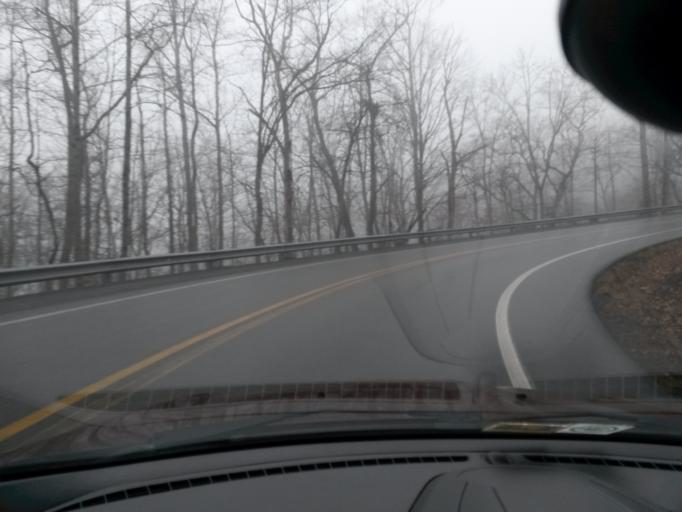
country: US
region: West Virginia
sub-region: Greenbrier County
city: Lewisburg
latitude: 37.8690
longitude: -80.5383
